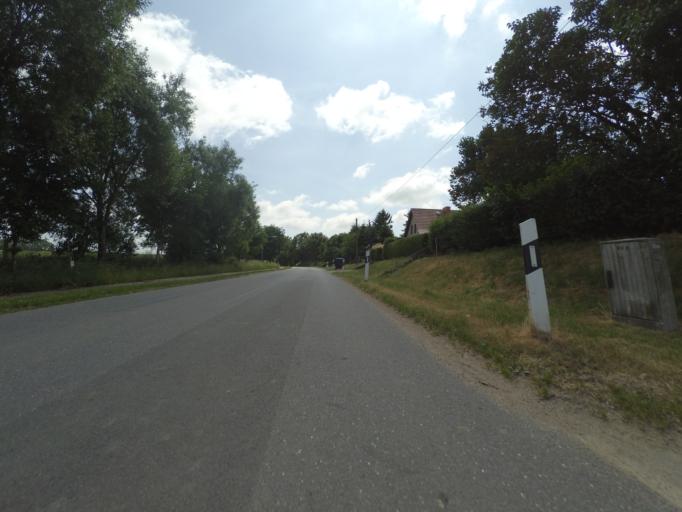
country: DE
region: Mecklenburg-Vorpommern
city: Neuburg
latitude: 53.4507
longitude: 11.9448
